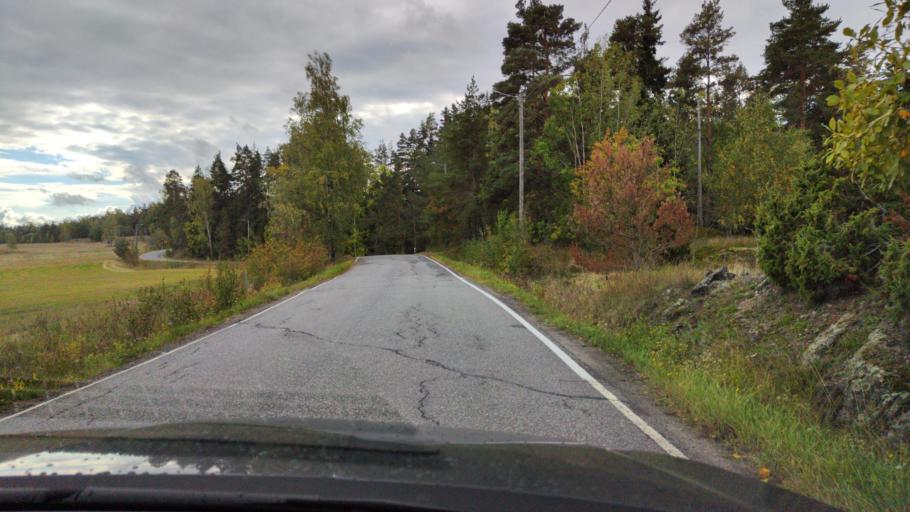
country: FI
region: Varsinais-Suomi
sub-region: Aboland-Turunmaa
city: Pargas
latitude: 60.3693
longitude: 22.2760
